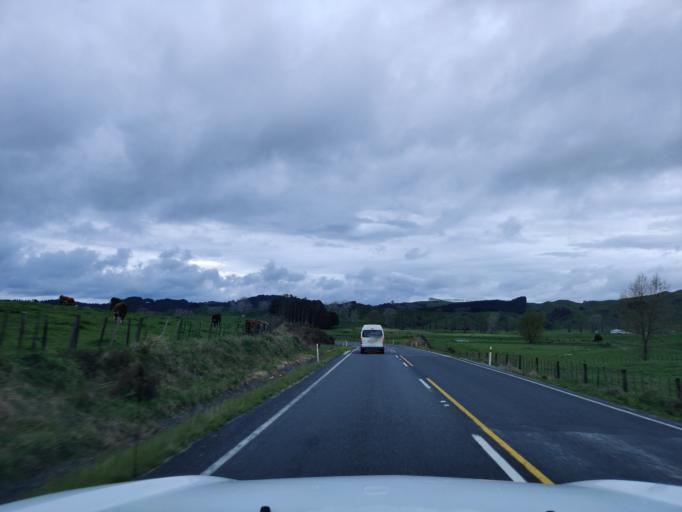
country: NZ
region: Waikato
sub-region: Otorohanga District
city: Otorohanga
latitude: -38.4582
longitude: 175.1677
